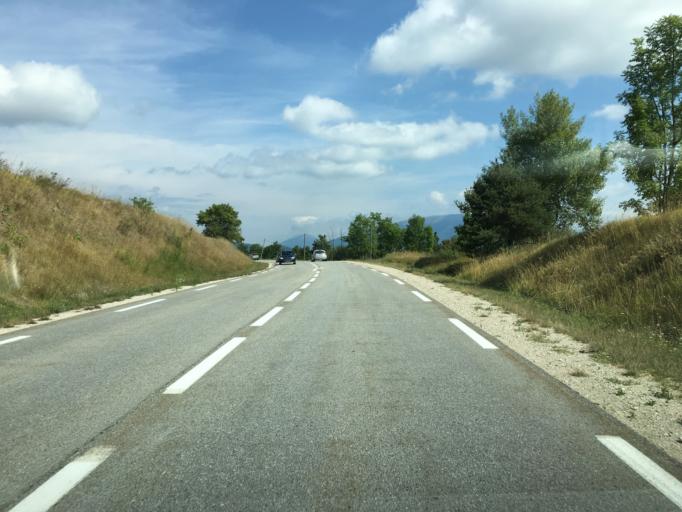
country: FR
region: Rhone-Alpes
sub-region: Departement de l'Isere
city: Mens
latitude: 44.8142
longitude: 5.6298
